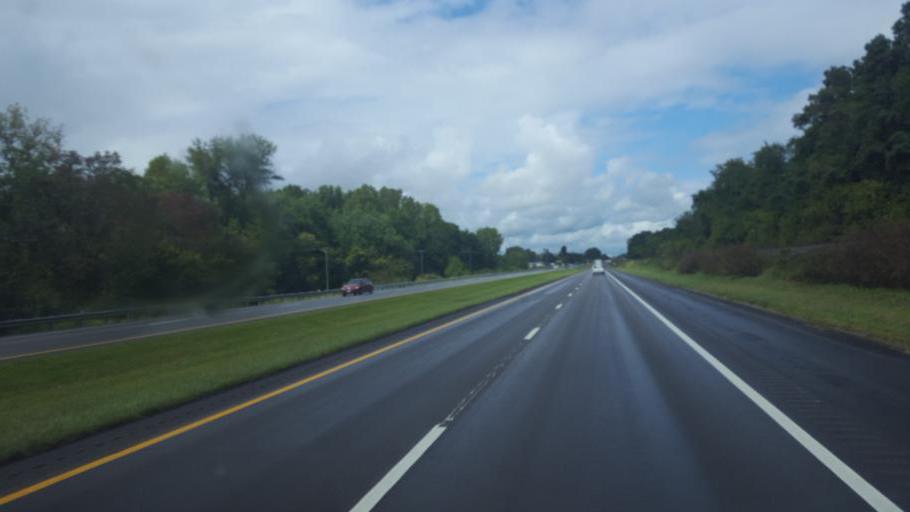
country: US
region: Ohio
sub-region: Scioto County
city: Lucasville
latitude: 38.8669
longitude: -82.9924
